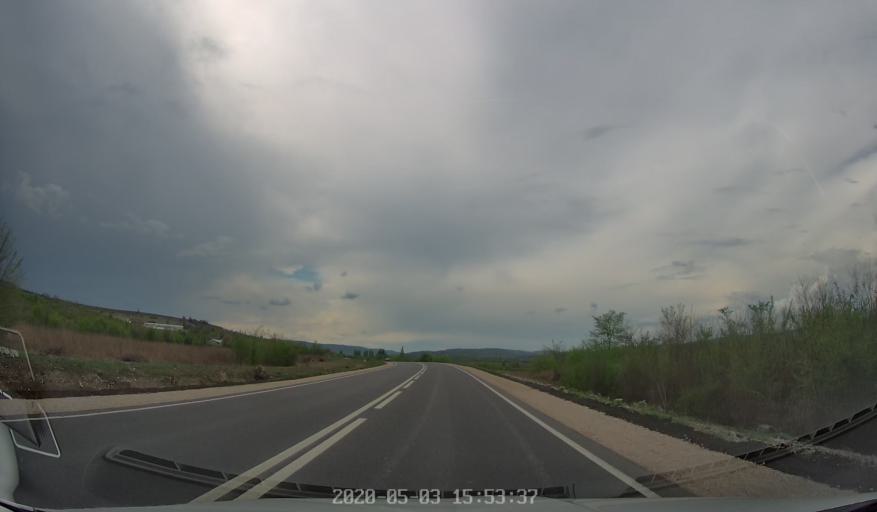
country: MD
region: Stinga Nistrului
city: Bucovat
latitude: 47.1734
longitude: 28.5147
